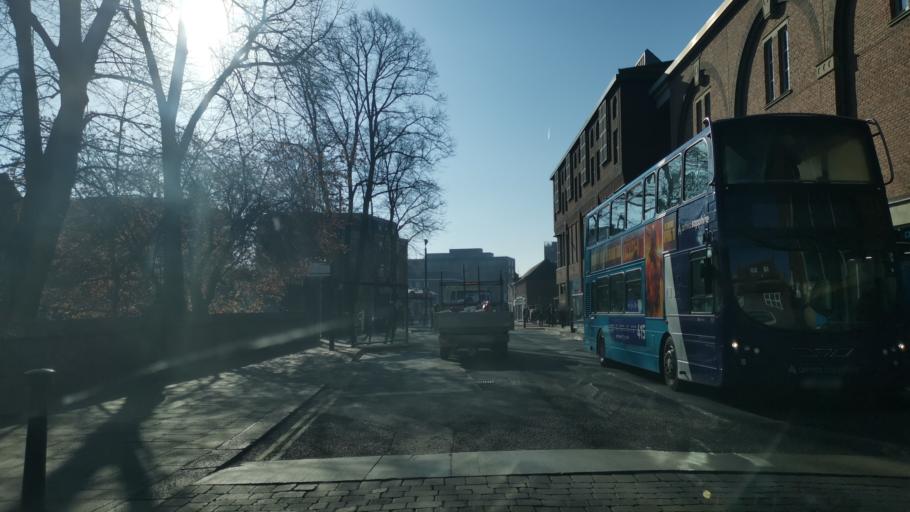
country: GB
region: England
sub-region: City of York
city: York
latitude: 53.9579
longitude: -1.0795
